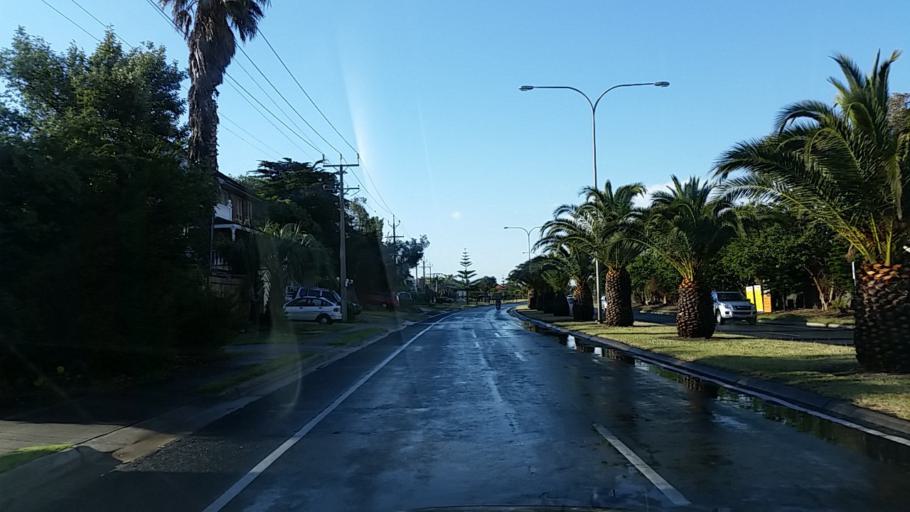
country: AU
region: South Australia
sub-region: Charles Sturt
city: Grange
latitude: -34.8908
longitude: 138.4875
